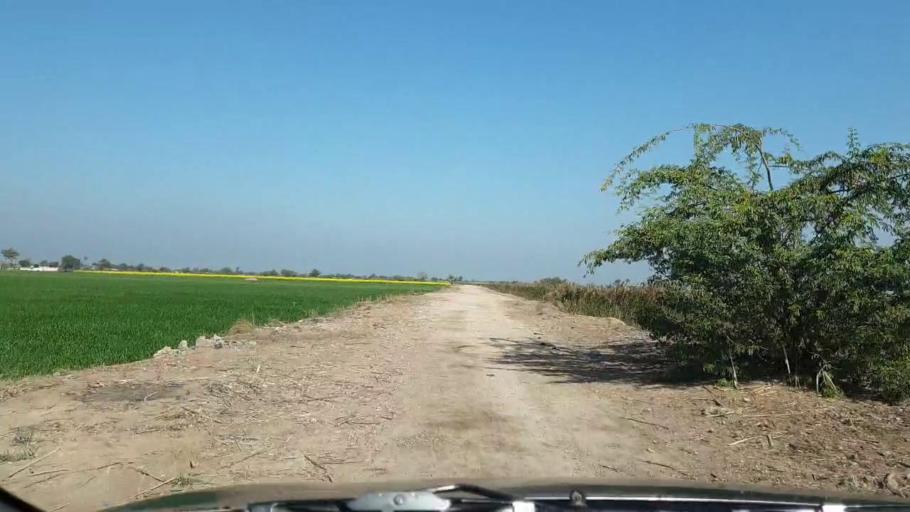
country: PK
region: Sindh
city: Sinjhoro
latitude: 25.9675
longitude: 68.7524
